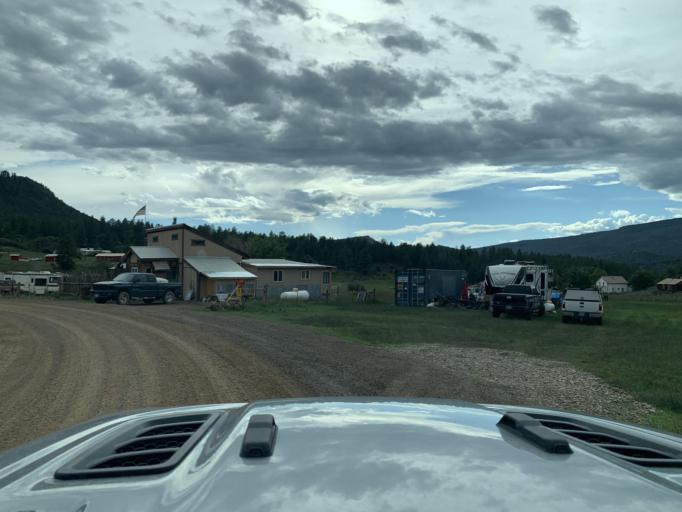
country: US
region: Colorado
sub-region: Archuleta County
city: Pagosa Springs
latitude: 37.2209
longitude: -107.1881
